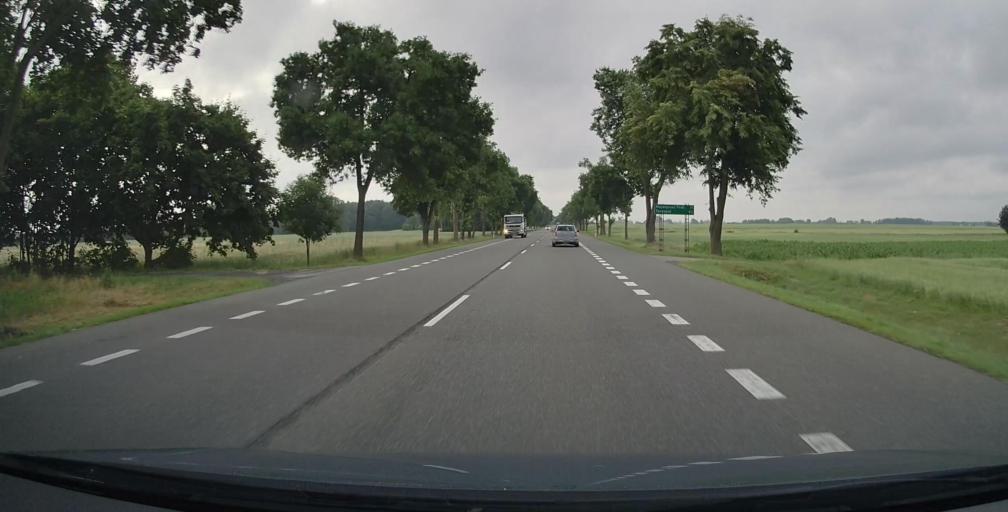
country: PL
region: Lublin Voivodeship
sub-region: Powiat lukowski
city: Trzebieszow
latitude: 52.0664
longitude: 22.5363
